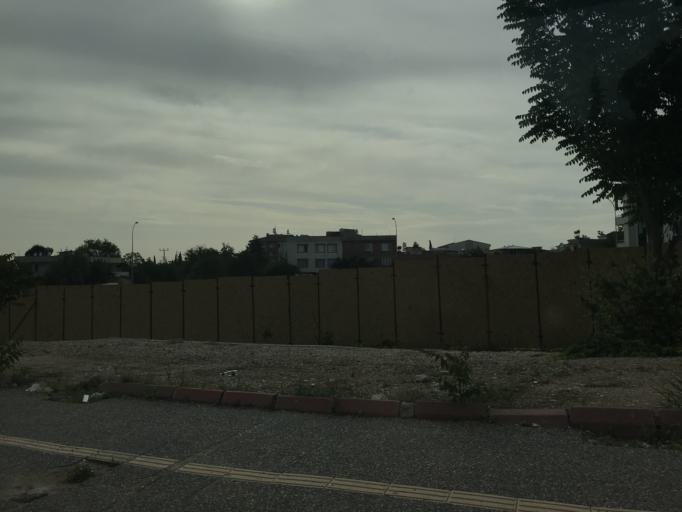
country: TR
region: Gaziantep
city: Sahinbey
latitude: 37.0602
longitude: 37.3332
